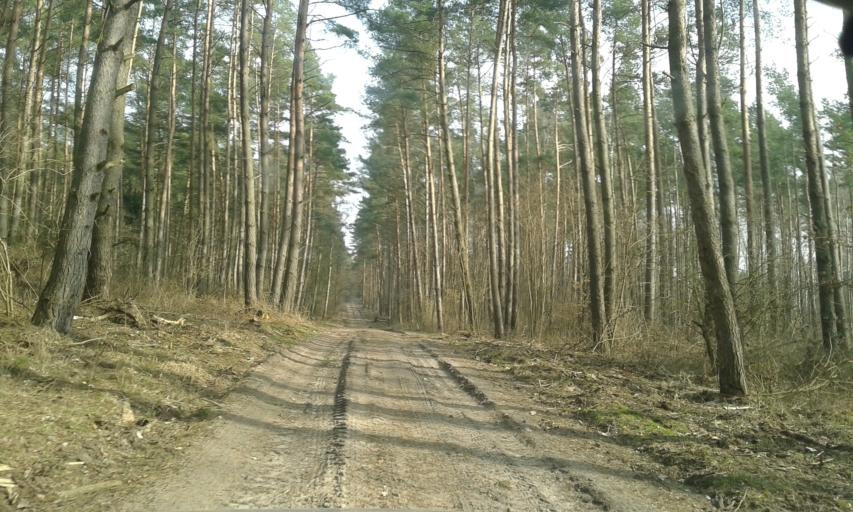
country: PL
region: West Pomeranian Voivodeship
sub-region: Powiat mysliborski
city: Barlinek
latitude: 53.0879
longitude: 15.2211
